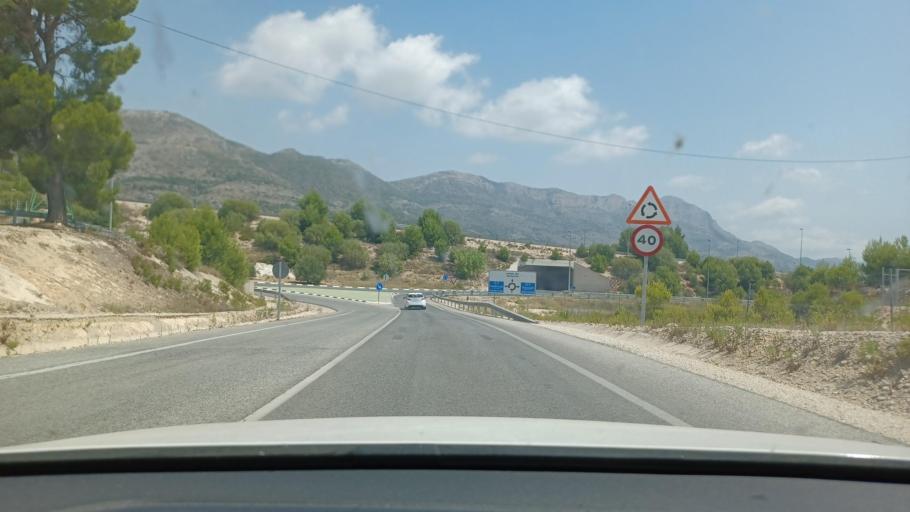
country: ES
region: Valencia
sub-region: Provincia de Alicante
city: Muro del Alcoy
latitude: 38.7928
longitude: -0.4497
